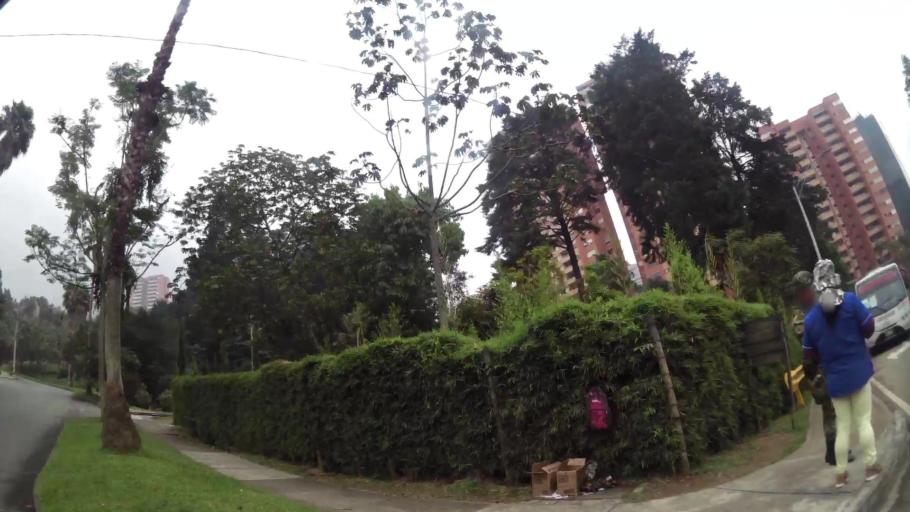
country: CO
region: Antioquia
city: Envigado
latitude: 6.1997
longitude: -75.5557
